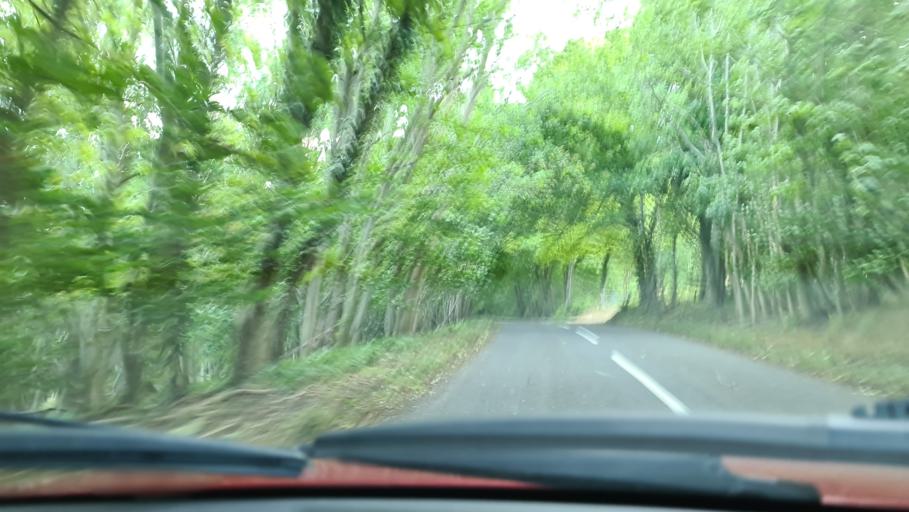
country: GB
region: England
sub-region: Buckinghamshire
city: Princes Risborough
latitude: 51.7331
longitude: -0.7888
